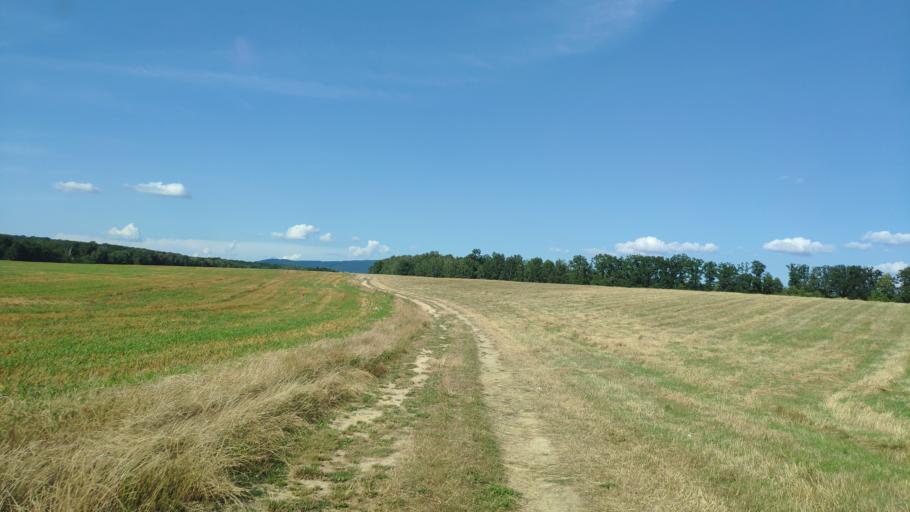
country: SK
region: Presovsky
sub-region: Okres Presov
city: Presov
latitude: 48.9087
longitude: 21.2921
